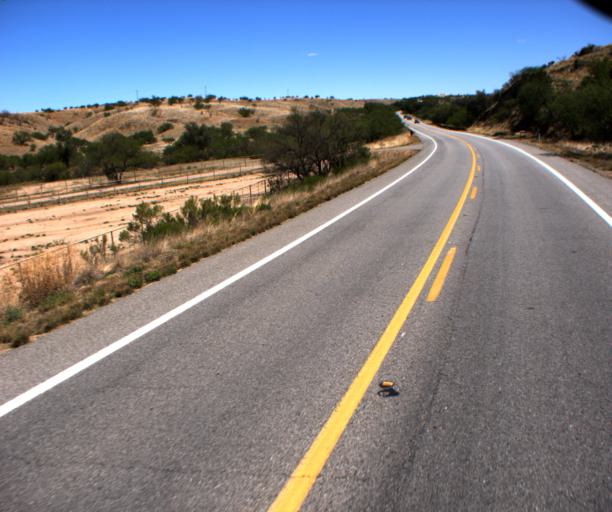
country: US
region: Arizona
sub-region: Santa Cruz County
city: Rio Rico
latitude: 31.4530
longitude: -110.8331
